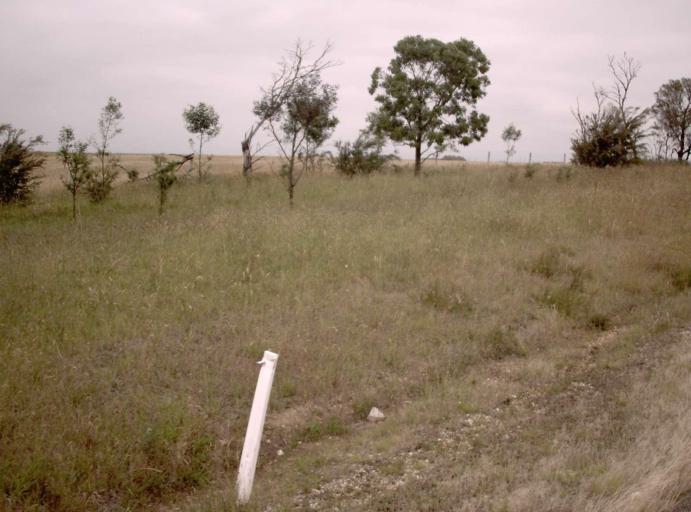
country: AU
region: Victoria
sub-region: Wellington
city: Heyfield
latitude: -38.1292
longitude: 146.7865
